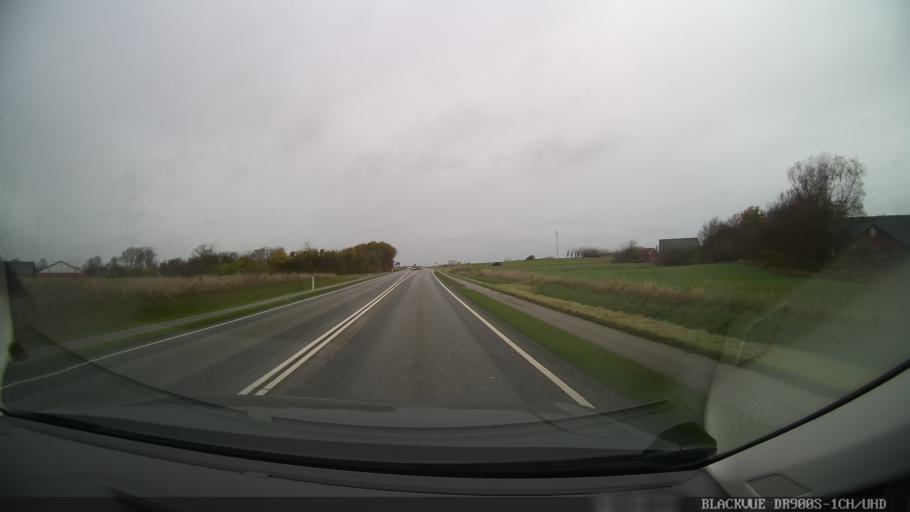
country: DK
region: North Denmark
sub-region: Thisted Kommune
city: Thisted
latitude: 56.8537
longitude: 8.6984
